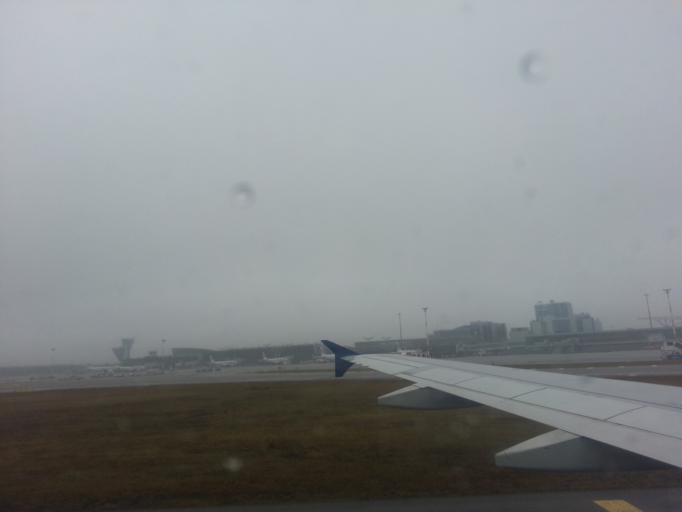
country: FI
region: Uusimaa
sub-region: Helsinki
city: Vantaa
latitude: 60.3193
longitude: 24.9567
